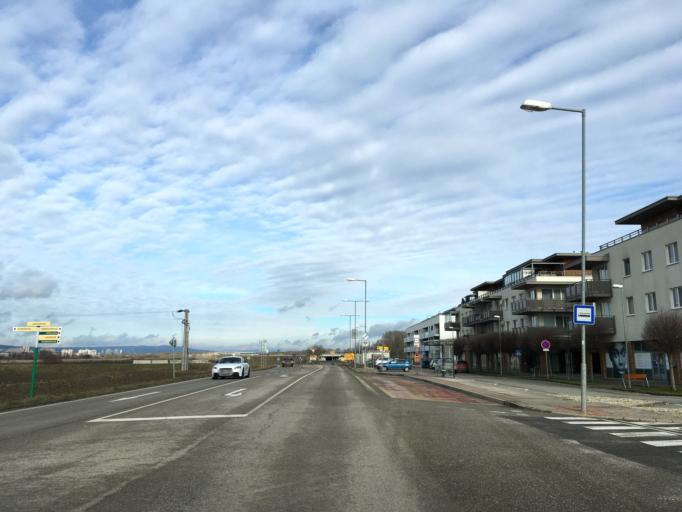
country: AT
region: Burgenland
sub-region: Politischer Bezirk Neusiedl am See
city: Deutsch Jahrndorf
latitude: 48.0704
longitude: 17.1174
